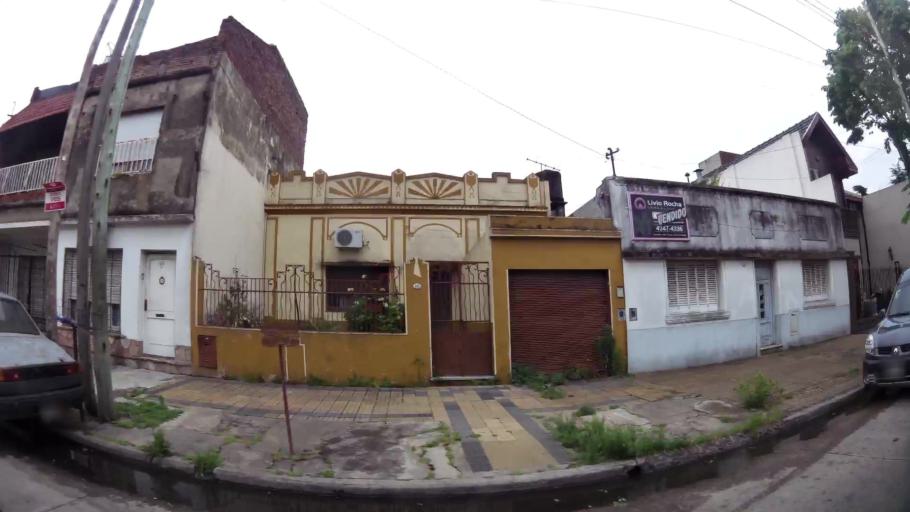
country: AR
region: Buenos Aires
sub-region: Partido de Lanus
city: Lanus
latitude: -34.6984
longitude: -58.3817
